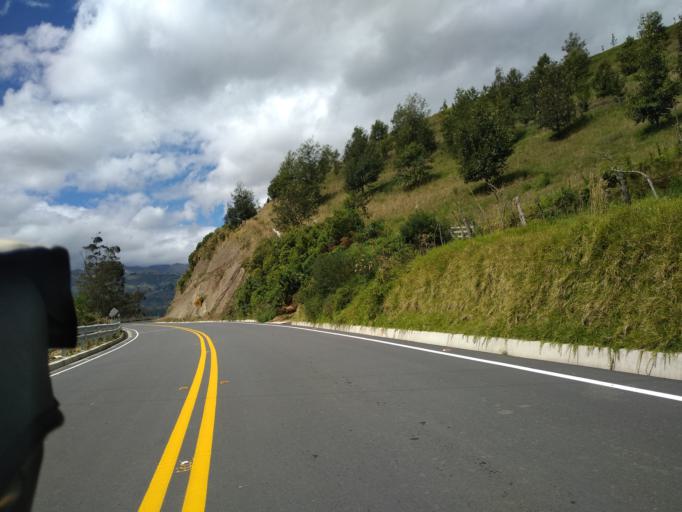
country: EC
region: Cotopaxi
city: Saquisili
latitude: -0.7242
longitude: -78.8925
